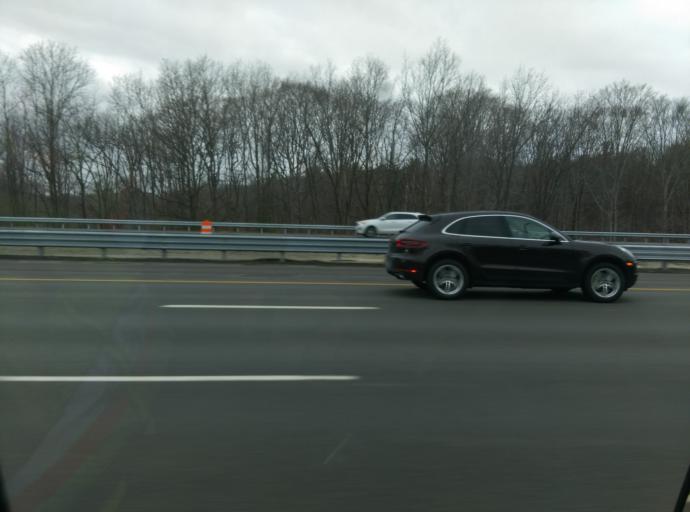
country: US
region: Massachusetts
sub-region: Essex County
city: Amesbury
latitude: 42.8480
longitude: -70.9009
